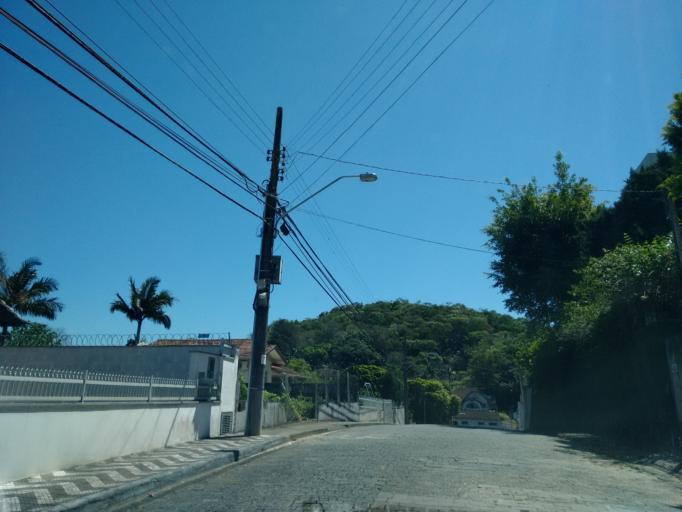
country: BR
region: Santa Catarina
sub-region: Blumenau
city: Blumenau
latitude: -26.8894
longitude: -49.0931
